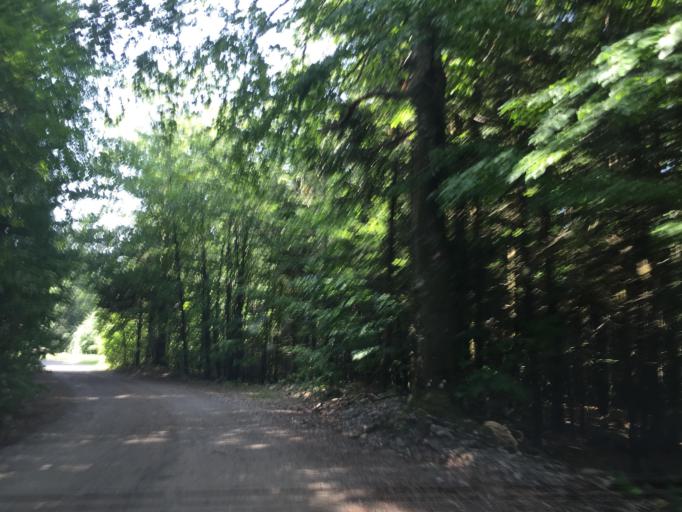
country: HR
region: Primorsko-Goranska
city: Podhum
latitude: 45.4440
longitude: 14.5572
